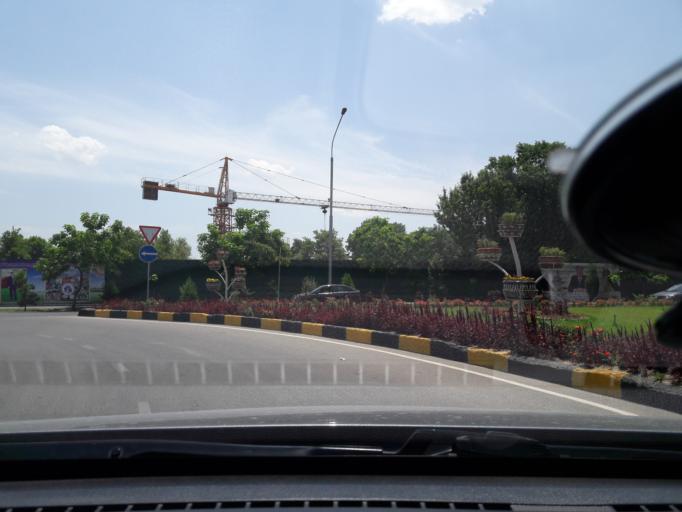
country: TJ
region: Dushanbe
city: Dushanbe
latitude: 38.5956
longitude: 68.7556
